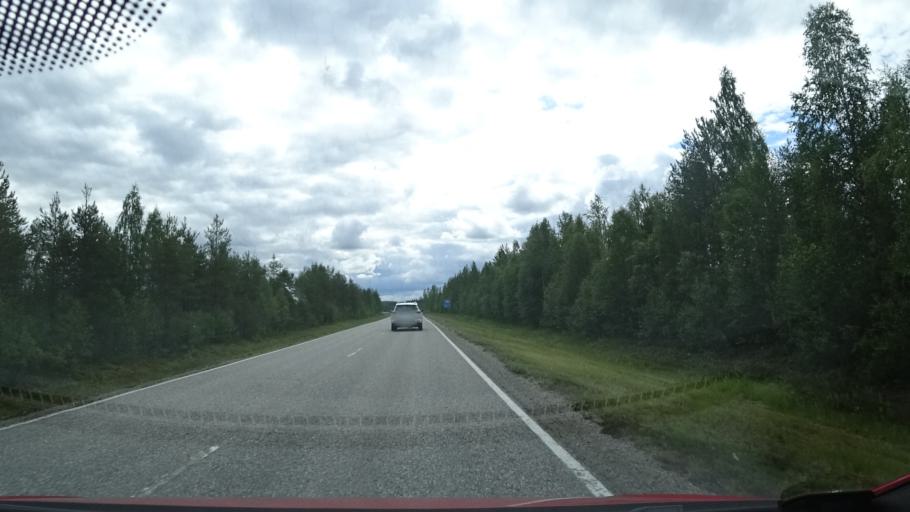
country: FI
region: Lapland
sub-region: Tunturi-Lappi
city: Kittilae
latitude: 67.4575
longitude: 24.9470
